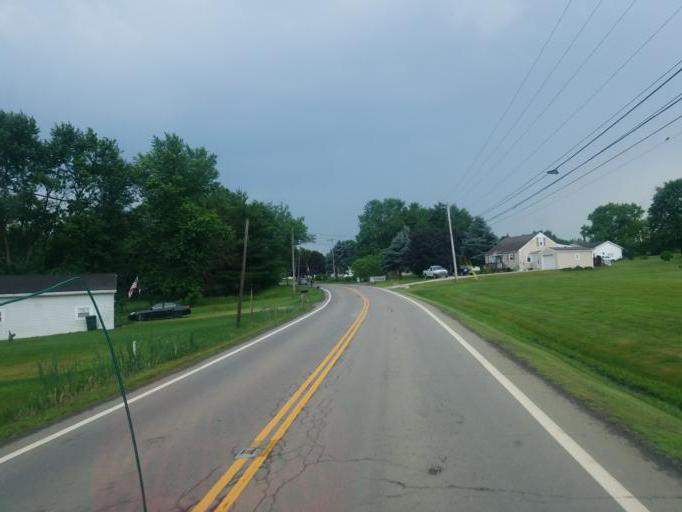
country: US
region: Ohio
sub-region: Wayne County
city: Doylestown
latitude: 40.9808
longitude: -81.7362
